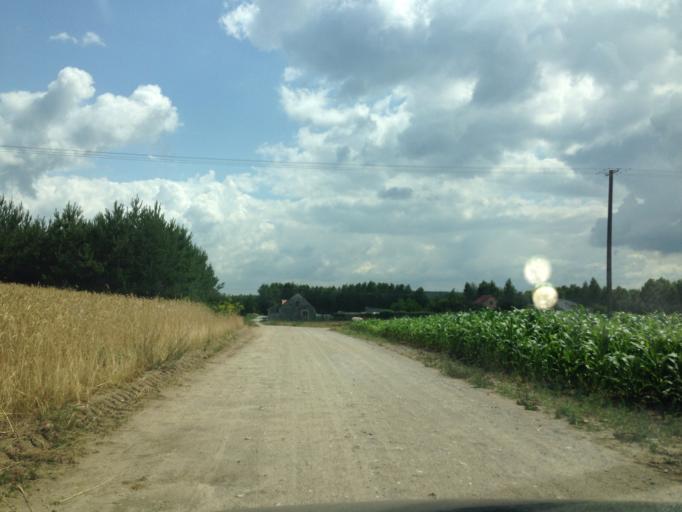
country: PL
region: Kujawsko-Pomorskie
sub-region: Powiat brodnicki
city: Gorzno
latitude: 53.2275
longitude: 19.6400
